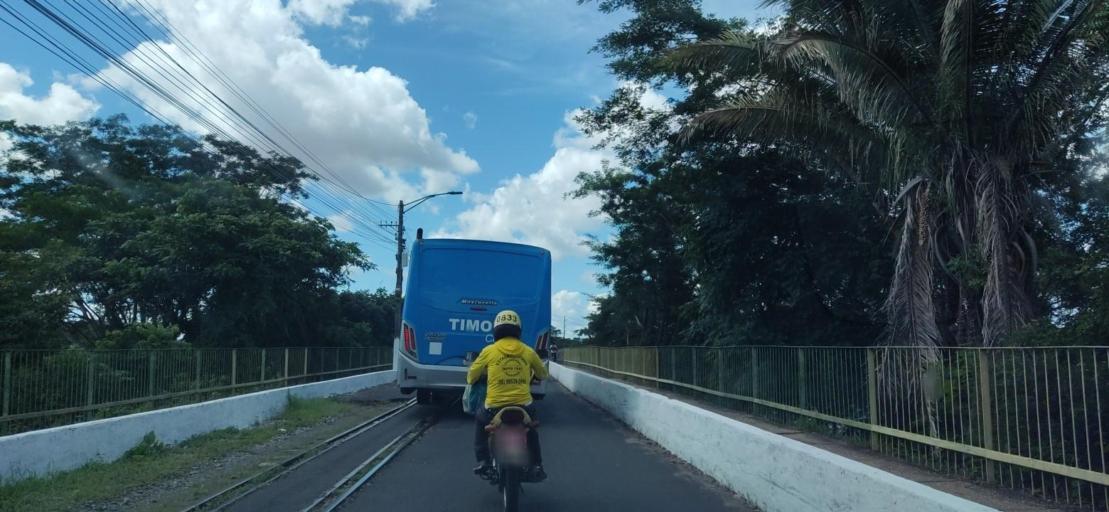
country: BR
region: Maranhao
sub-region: Timon
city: Timon
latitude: -5.0881
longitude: -42.8259
